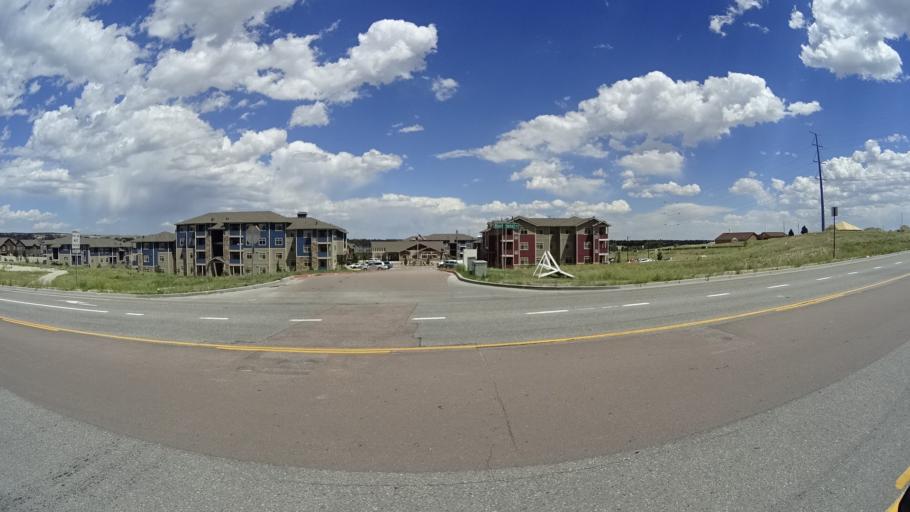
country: US
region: Colorado
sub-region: El Paso County
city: Black Forest
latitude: 38.9425
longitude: -104.7011
